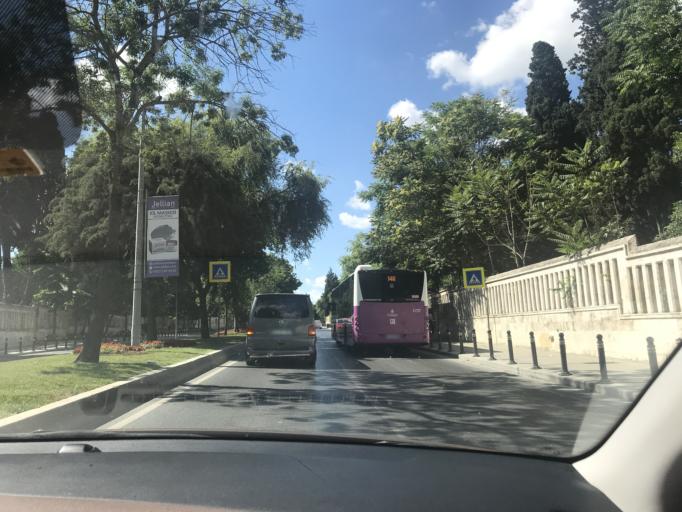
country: TR
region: Istanbul
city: UEskuedar
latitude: 41.0096
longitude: 29.0225
